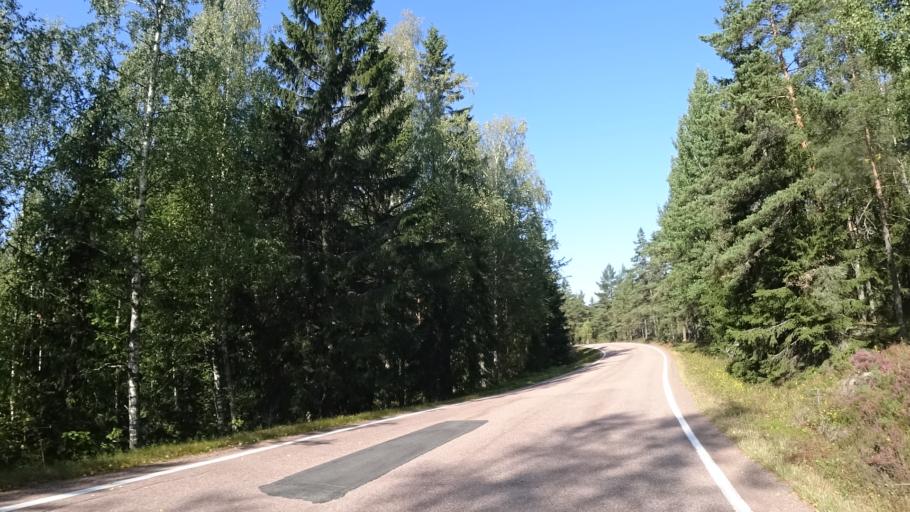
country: FI
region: Kymenlaakso
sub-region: Kotka-Hamina
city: Virolahti
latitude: 60.5204
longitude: 27.5247
